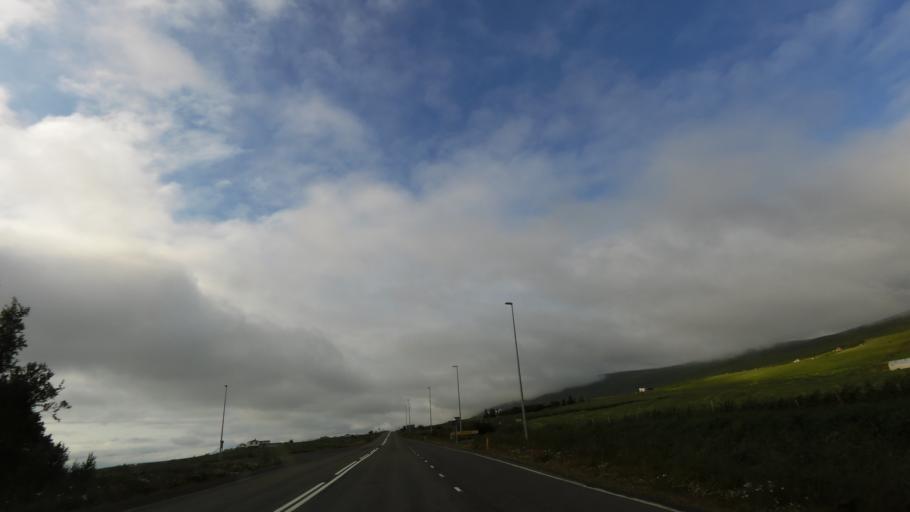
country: IS
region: Northeast
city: Akureyri
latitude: 65.7494
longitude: -18.0749
